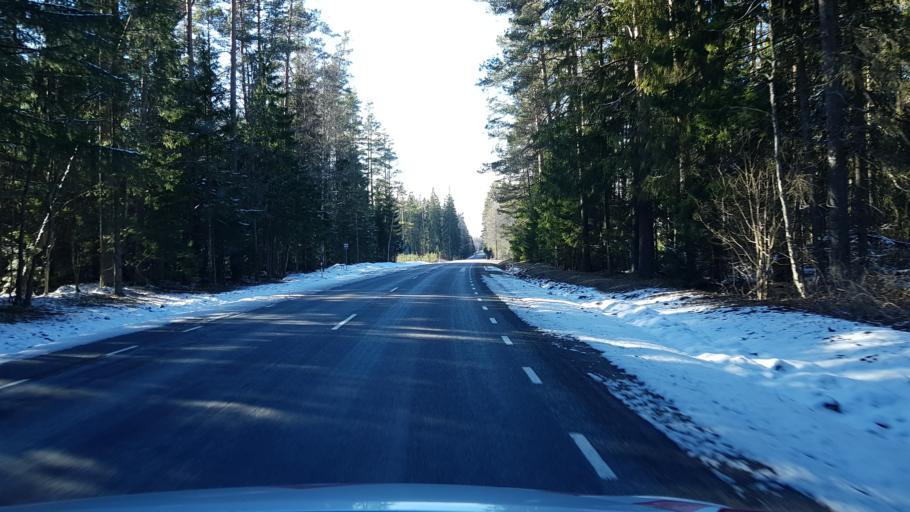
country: EE
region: Laeaene-Virumaa
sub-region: Tapa vald
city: Tapa
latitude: 59.4279
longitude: 25.9785
